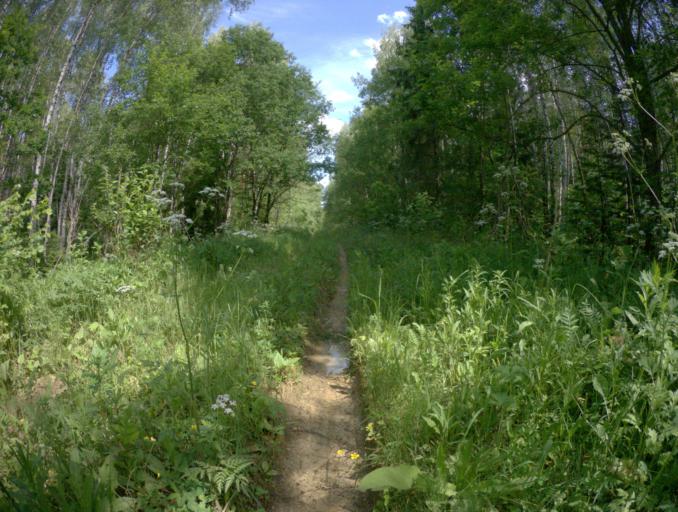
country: RU
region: Vladimir
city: Stavrovo
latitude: 56.3215
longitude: 39.9477
